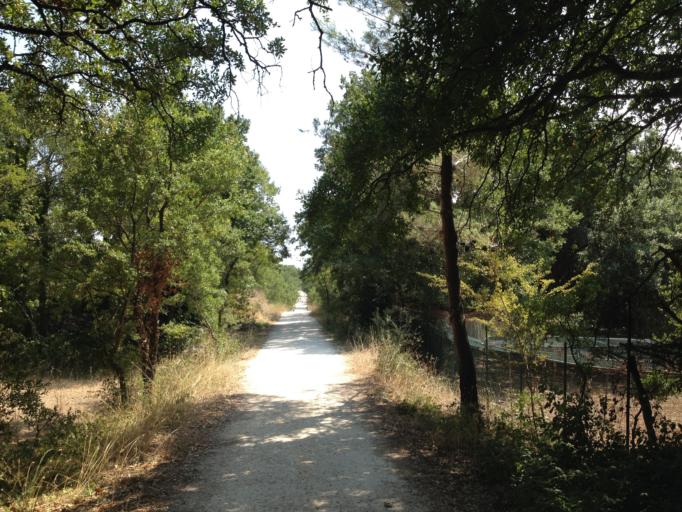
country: IT
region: Apulia
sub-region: Provincia di Brindisi
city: Cisternino
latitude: 40.7125
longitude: 17.4088
